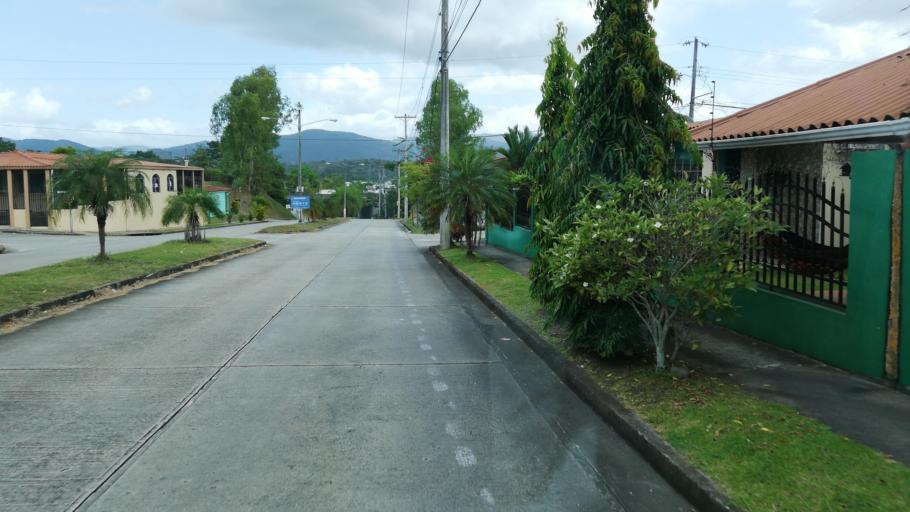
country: PA
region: Panama
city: San Miguelito
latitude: 9.0777
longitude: -79.4572
